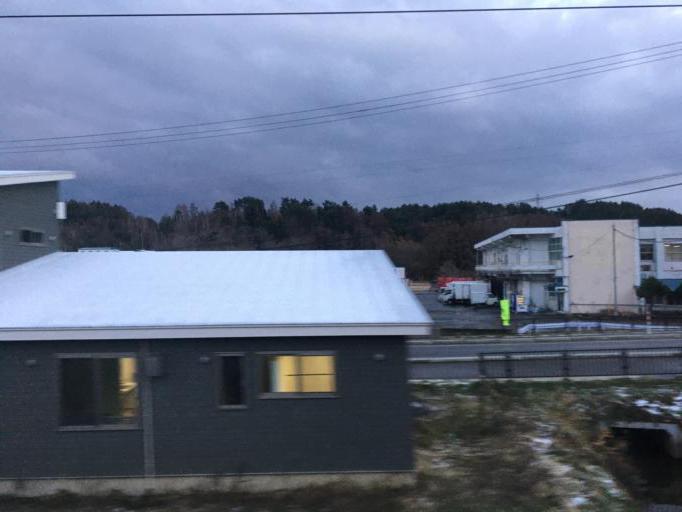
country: JP
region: Aomori
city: Aomori Shi
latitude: 40.8229
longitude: 140.6585
